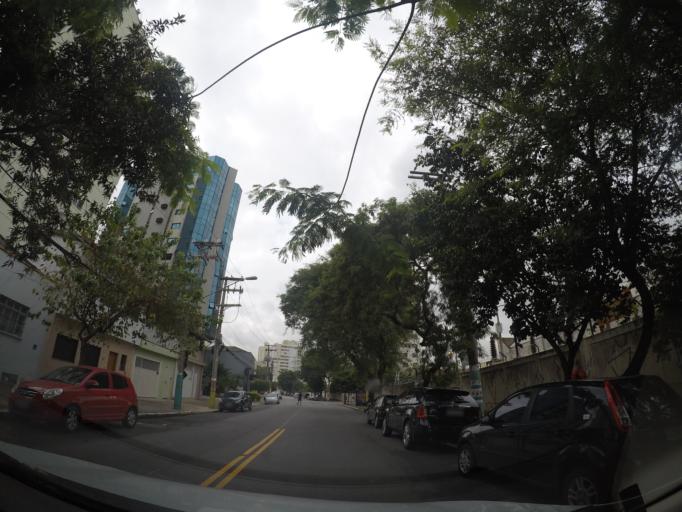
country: BR
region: Sao Paulo
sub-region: Sao Paulo
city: Sao Paulo
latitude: -23.5588
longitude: -46.6037
